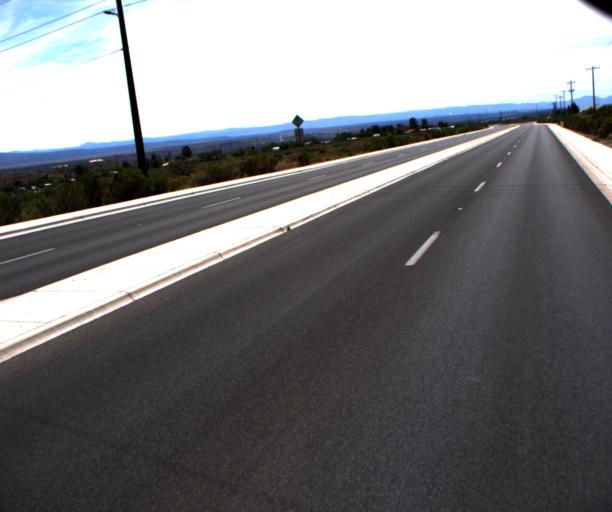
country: US
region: Arizona
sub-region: Yavapai County
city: Clarkdale
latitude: 34.7608
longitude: -112.0617
